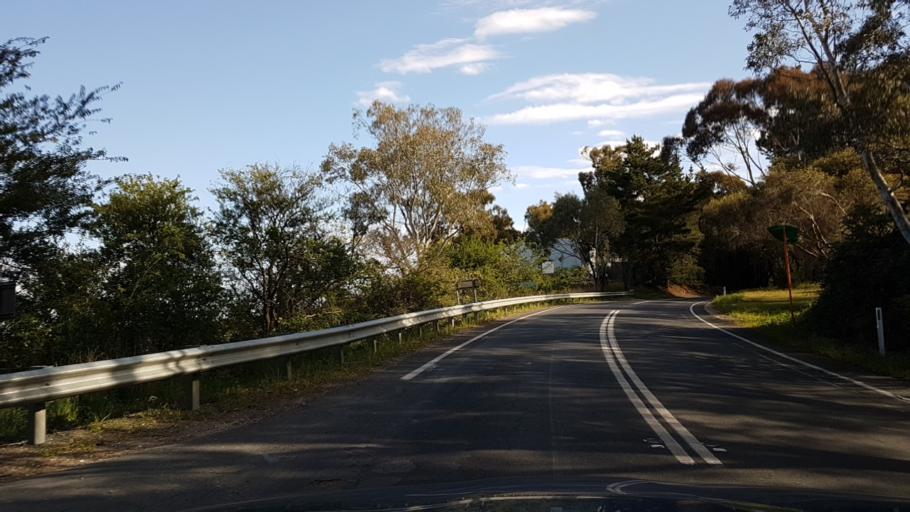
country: AU
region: South Australia
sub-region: Adelaide Hills
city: Lobethal
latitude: -34.8783
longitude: 138.8919
